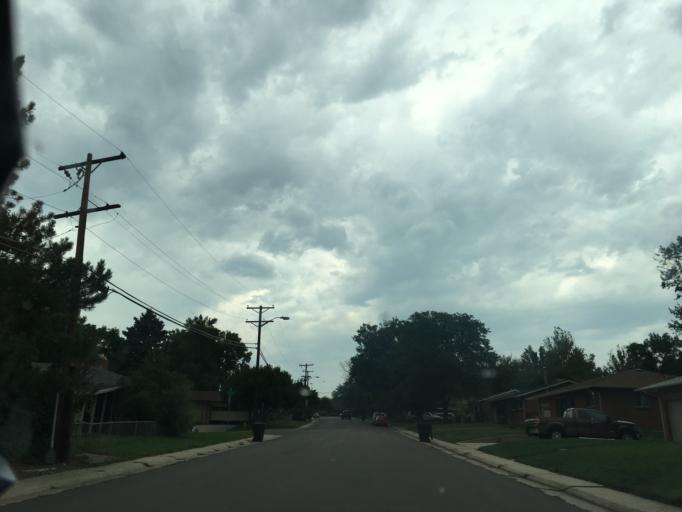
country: US
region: Colorado
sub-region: Arapahoe County
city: Sheridan
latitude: 39.6586
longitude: -105.0388
